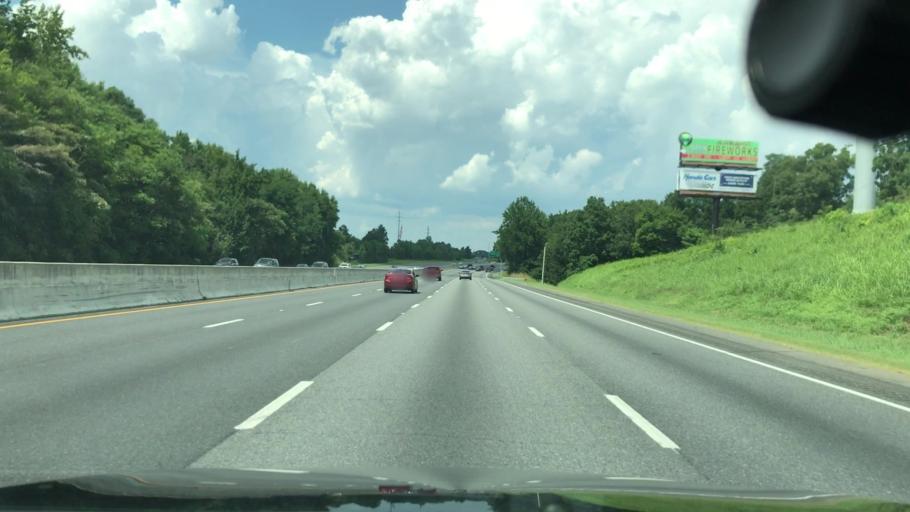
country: US
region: South Carolina
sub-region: York County
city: Fort Mill
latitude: 35.0533
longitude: -80.9582
